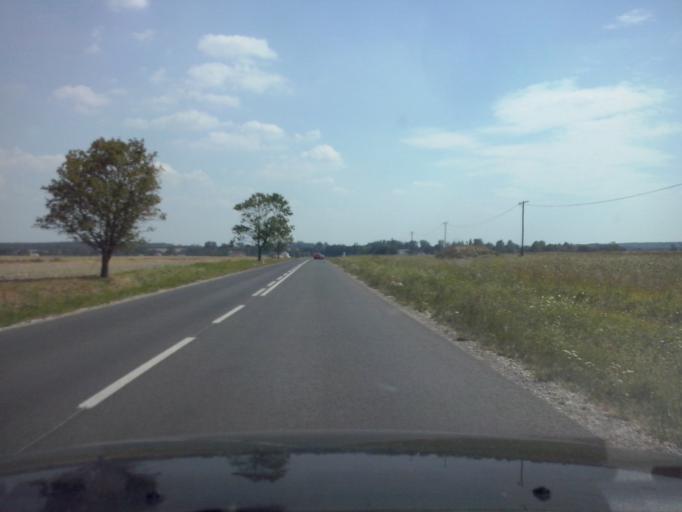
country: PL
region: Swietokrzyskie
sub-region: Powiat buski
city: Gnojno
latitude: 50.5977
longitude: 20.8721
